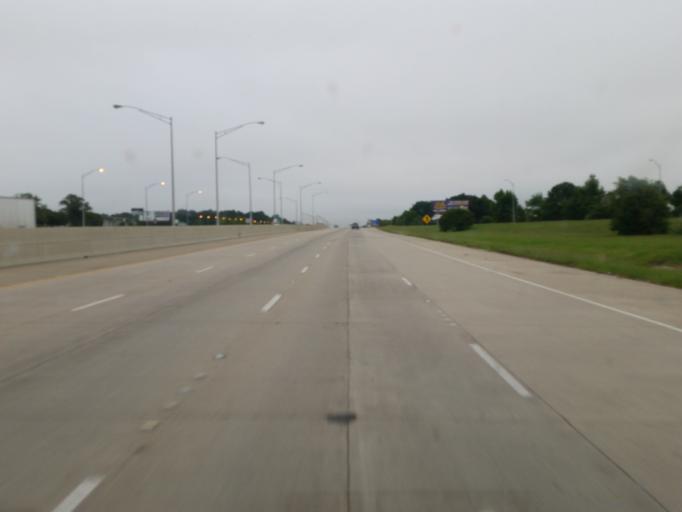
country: US
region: Louisiana
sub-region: Caddo Parish
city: Shreveport
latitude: 32.4563
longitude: -93.8439
